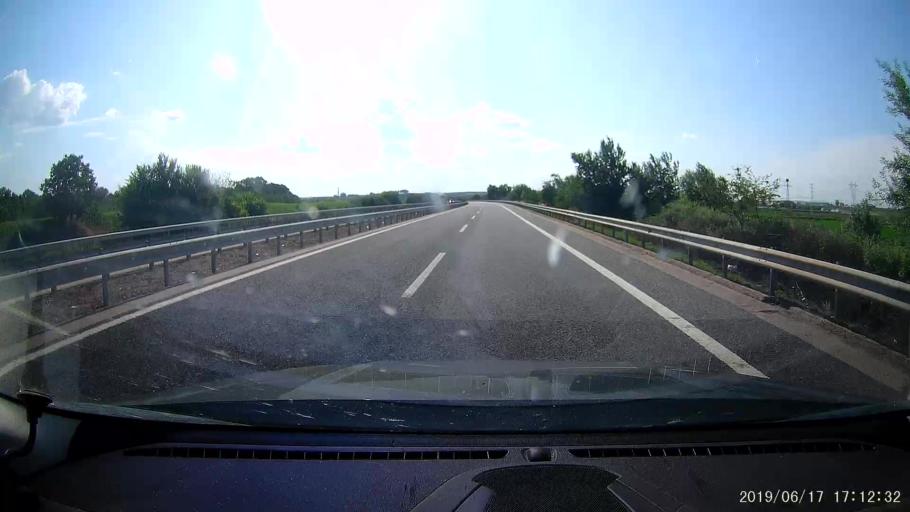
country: TR
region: Edirne
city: Edirne
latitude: 41.7001
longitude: 26.5605
